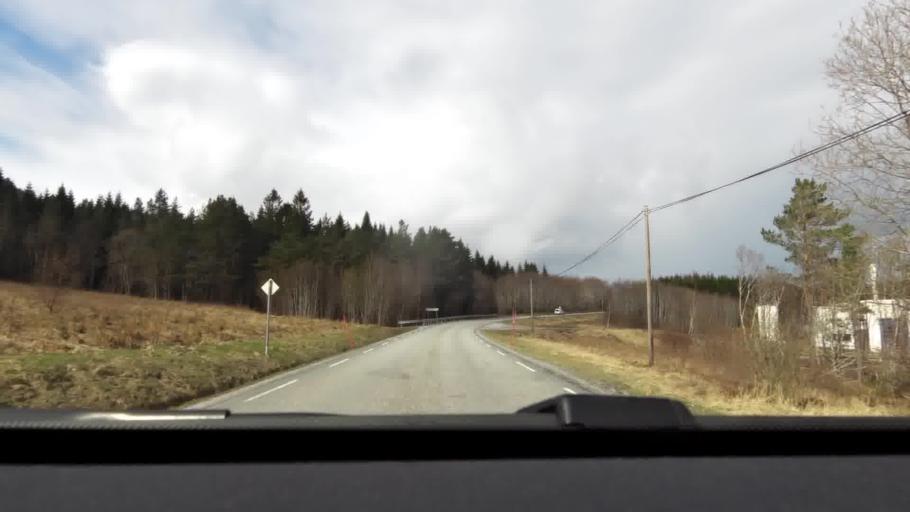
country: NO
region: More og Romsdal
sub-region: Averoy
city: Bruhagen
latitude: 63.1037
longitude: 7.6276
